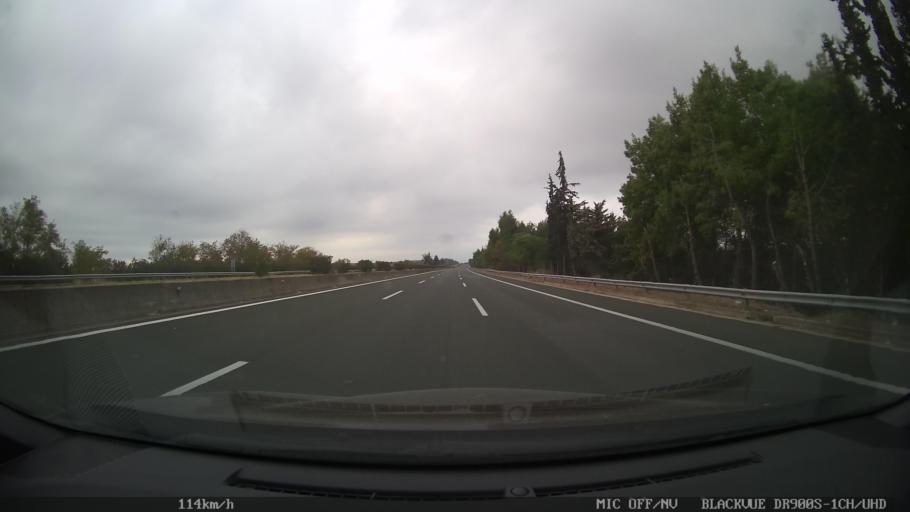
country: GR
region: Central Macedonia
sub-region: Nomos Pierias
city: Kitros
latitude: 40.3605
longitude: 22.6018
